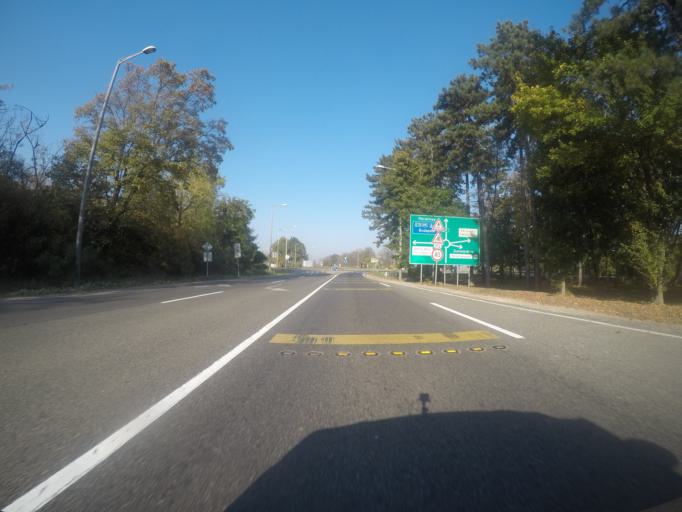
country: HU
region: Fejer
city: Racalmas
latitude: 46.9979
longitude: 18.9295
